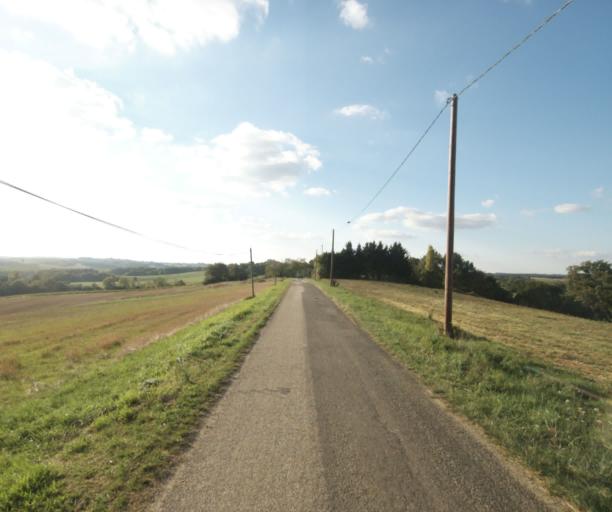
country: FR
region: Midi-Pyrenees
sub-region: Departement du Gers
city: Eauze
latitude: 43.7491
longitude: 0.1159
